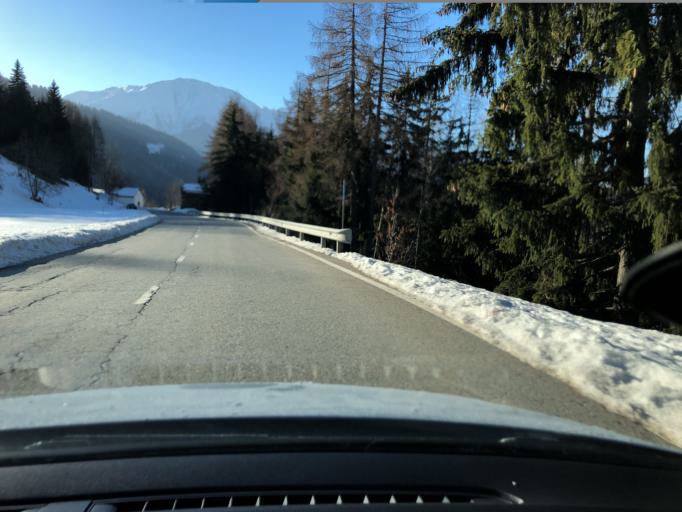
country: CH
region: Valais
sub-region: Goms District
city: Fiesch
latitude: 46.4197
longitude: 8.1523
